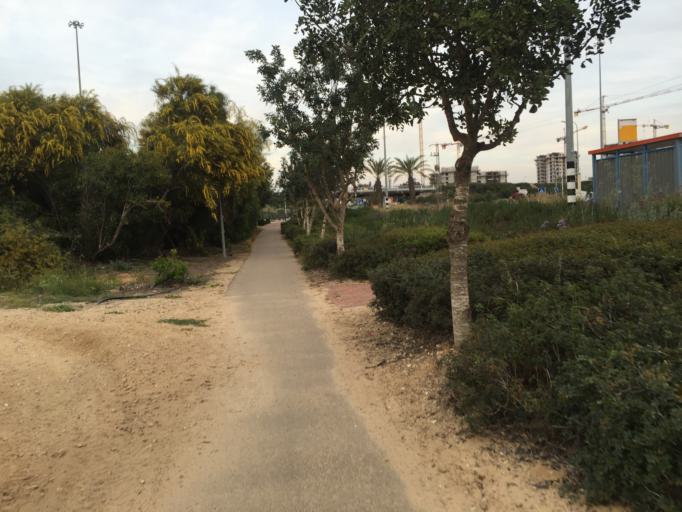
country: IL
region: Haifa
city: Qesarya
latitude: 32.5048
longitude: 34.9123
